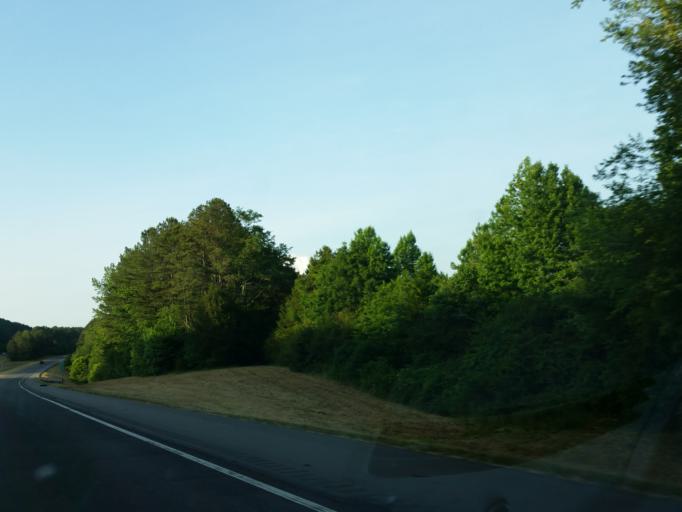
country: US
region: Alabama
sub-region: DeKalb County
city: Henagar
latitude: 34.6152
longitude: -85.6328
